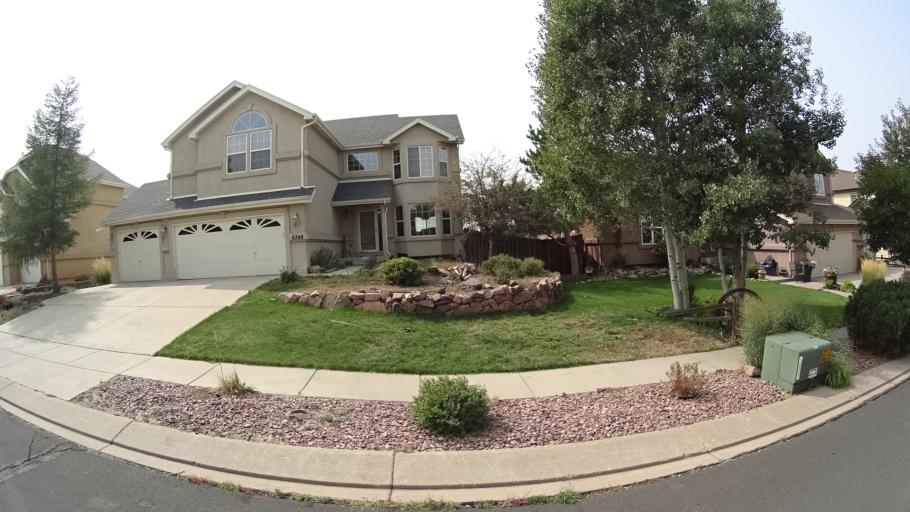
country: US
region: Colorado
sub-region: El Paso County
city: Cimarron Hills
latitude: 38.9234
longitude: -104.7430
